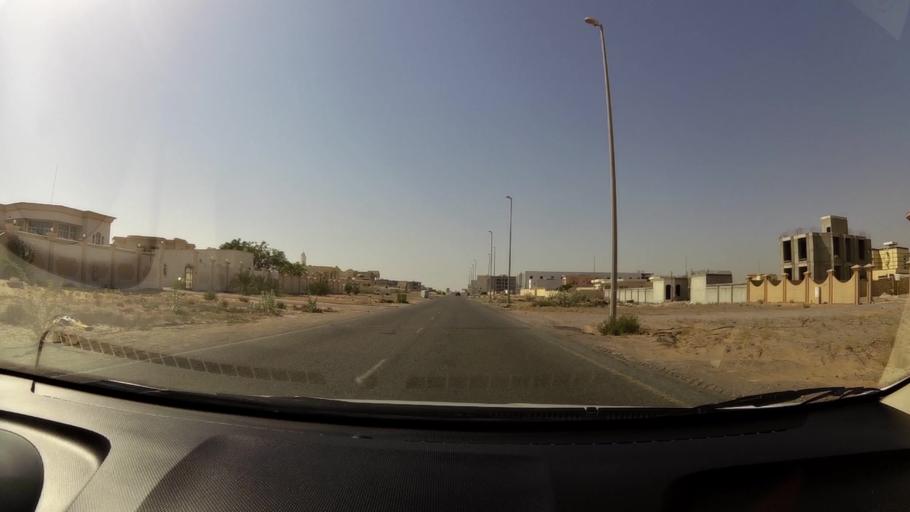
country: AE
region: Umm al Qaywayn
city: Umm al Qaywayn
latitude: 25.4888
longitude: 55.6008
